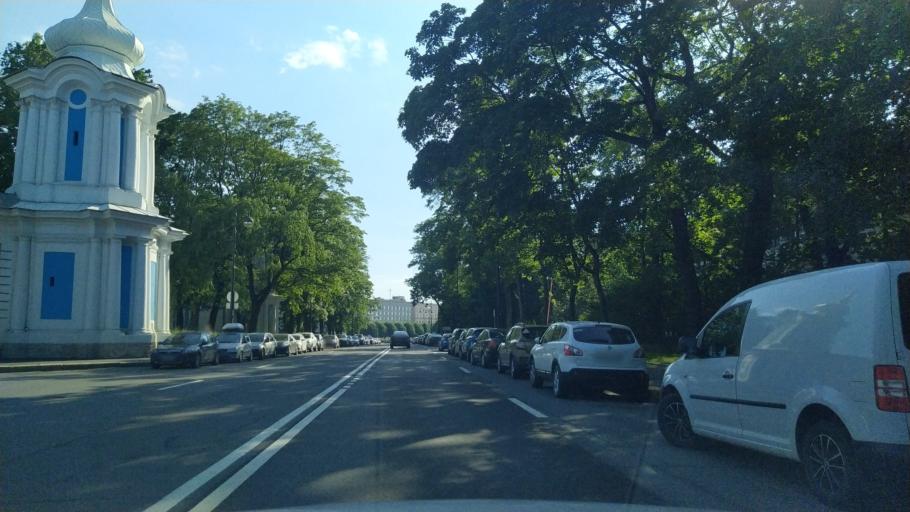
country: RU
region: Leningrad
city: Finlyandskiy
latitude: 59.9506
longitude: 30.3938
